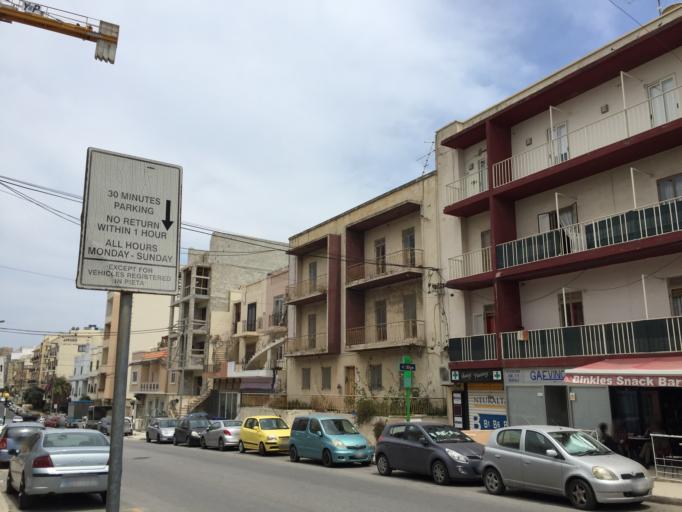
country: MT
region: Tal-Pieta
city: Pieta
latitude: 35.8894
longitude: 14.4907
